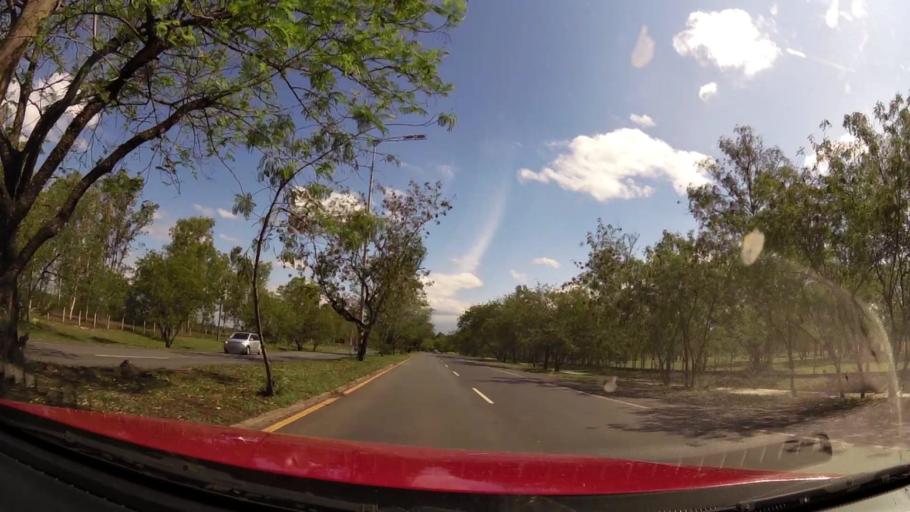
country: PY
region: Central
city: Fernando de la Mora
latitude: -25.2686
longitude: -57.5370
